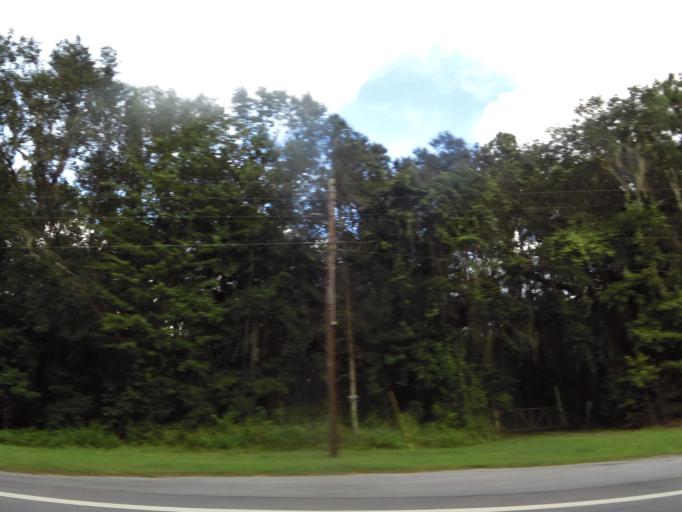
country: US
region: Georgia
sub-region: Liberty County
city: Midway
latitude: 31.7932
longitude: -81.4316
